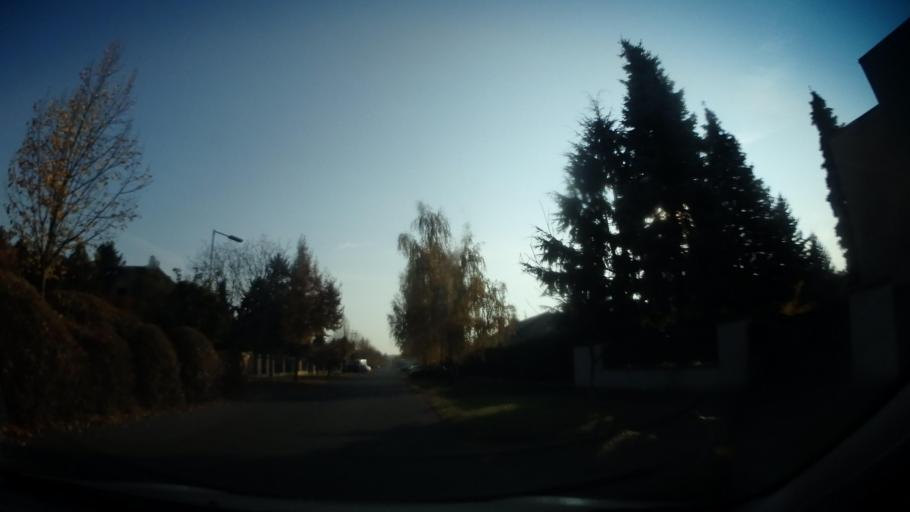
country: CZ
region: Central Bohemia
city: Sestajovice
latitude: 50.1015
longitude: 14.6793
